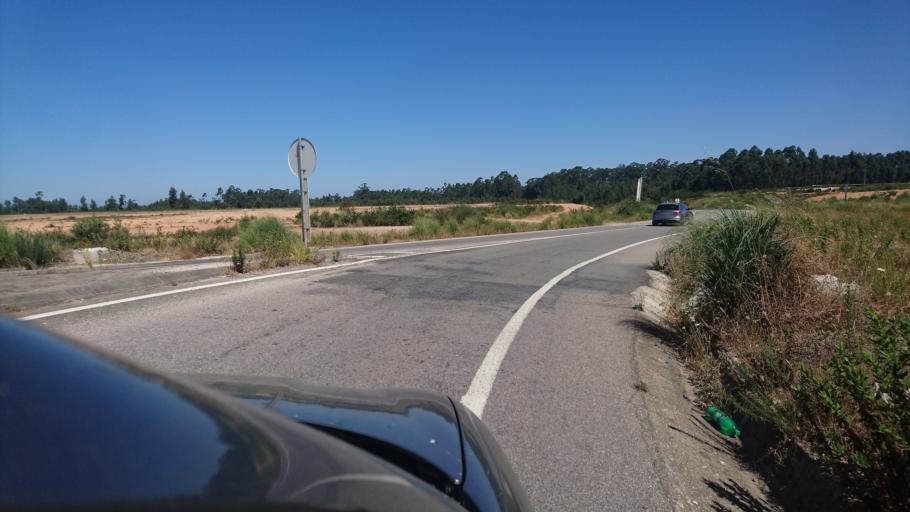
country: PT
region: Aveiro
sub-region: Santa Maria da Feira
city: Rio Meao
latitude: 40.9392
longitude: -8.5813
